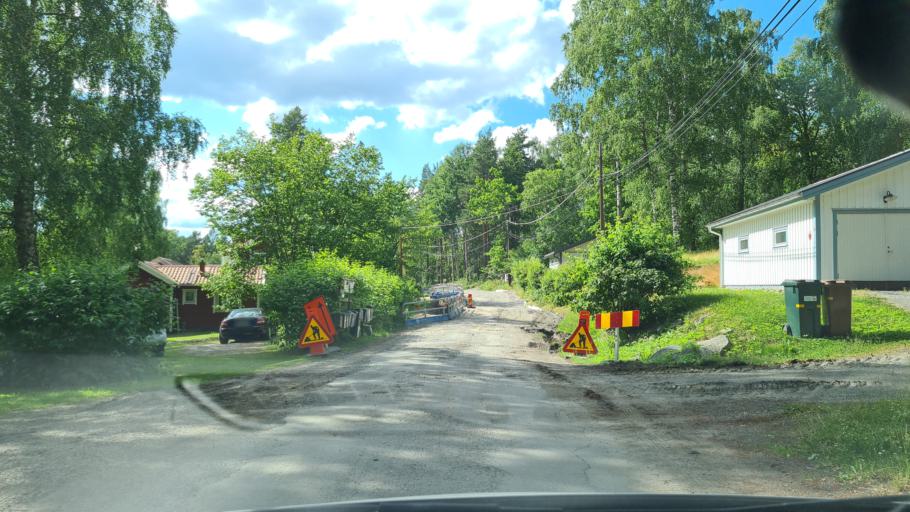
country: SE
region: Stockholm
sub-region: Vaxholms Kommun
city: Vaxholm
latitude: 59.4097
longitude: 18.3834
